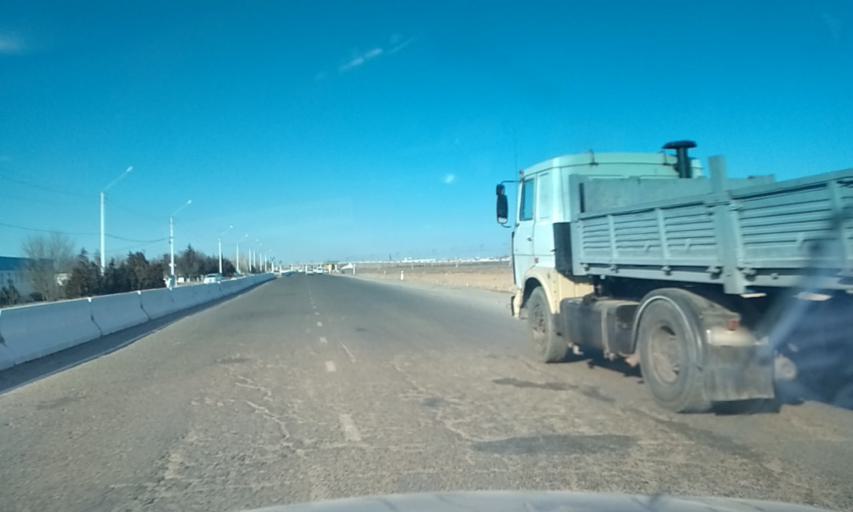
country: UZ
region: Sirdaryo
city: Guliston
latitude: 40.4658
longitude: 68.7721
